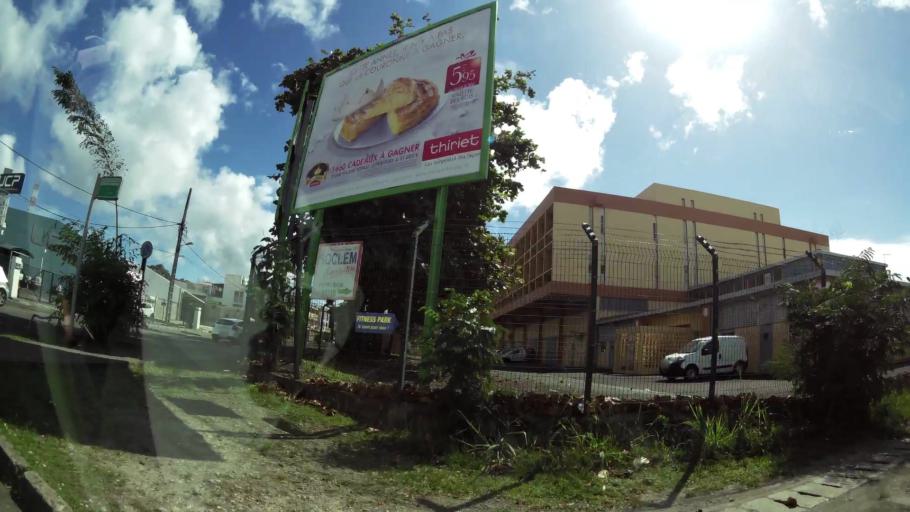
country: GP
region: Guadeloupe
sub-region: Guadeloupe
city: Pointe-a-Pitre
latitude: 16.2477
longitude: -61.5398
